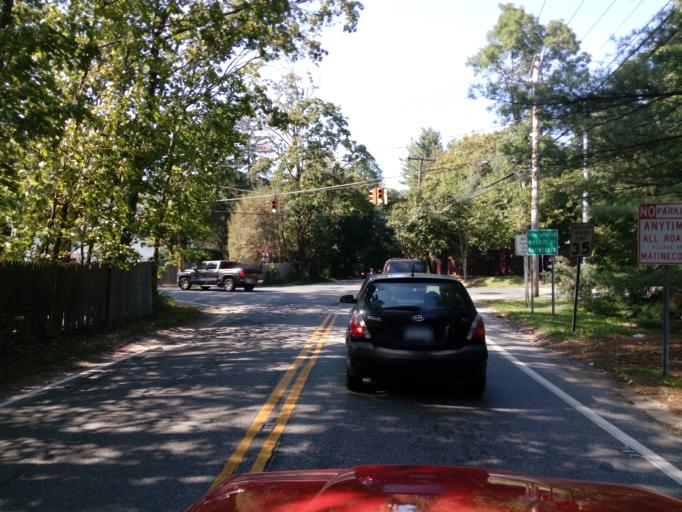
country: US
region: New York
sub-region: Nassau County
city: Upper Brookville
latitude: 40.8445
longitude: -73.5856
